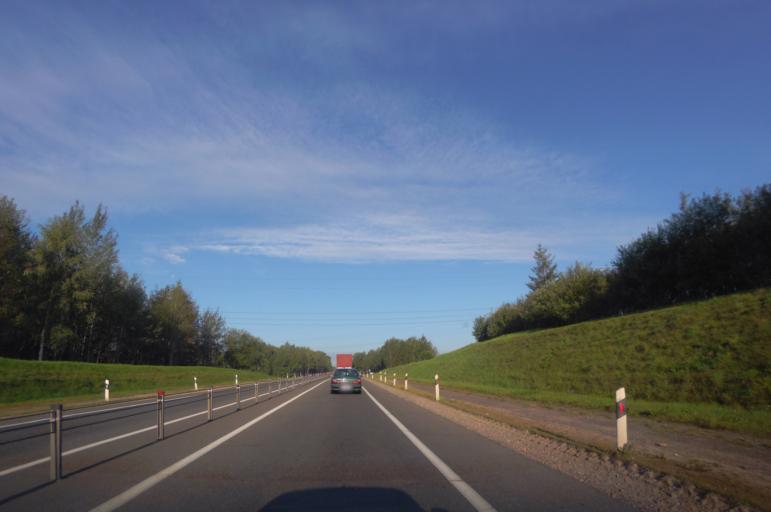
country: BY
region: Minsk
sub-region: Smalyavitski Rayon
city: Usjazh
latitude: 54.0297
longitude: 27.9877
